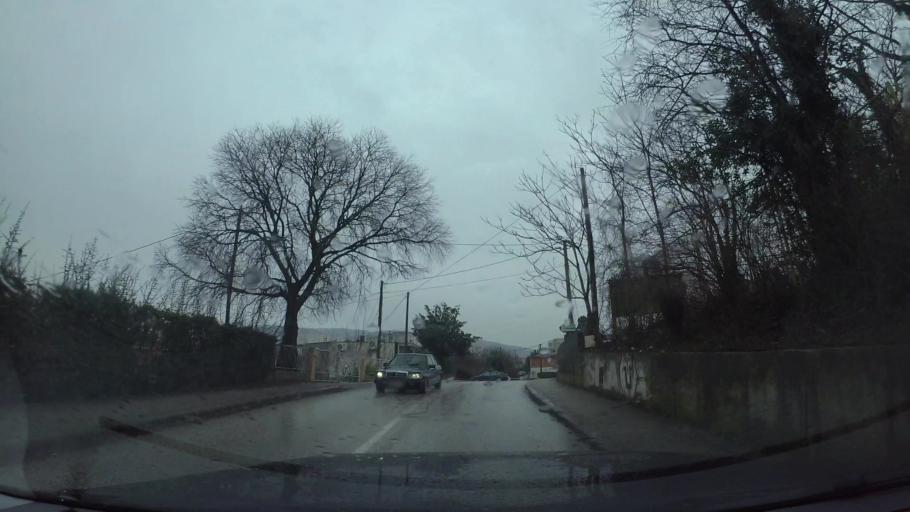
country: BA
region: Federation of Bosnia and Herzegovina
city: Cim
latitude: 43.3466
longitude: 17.7894
